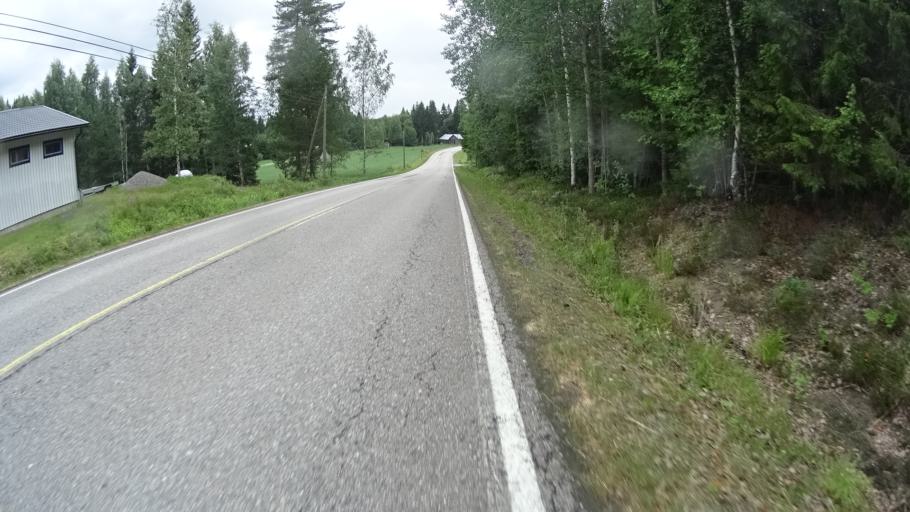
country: FI
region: Uusimaa
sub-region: Helsinki
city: Karkkila
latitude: 60.5720
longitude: 24.3238
